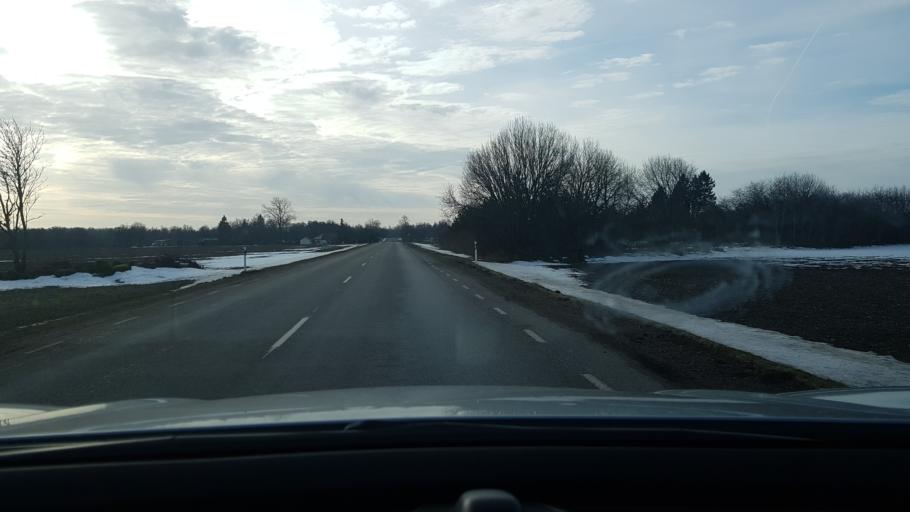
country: EE
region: Saare
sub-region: Kuressaare linn
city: Kuressaare
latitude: 58.3128
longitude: 22.5435
